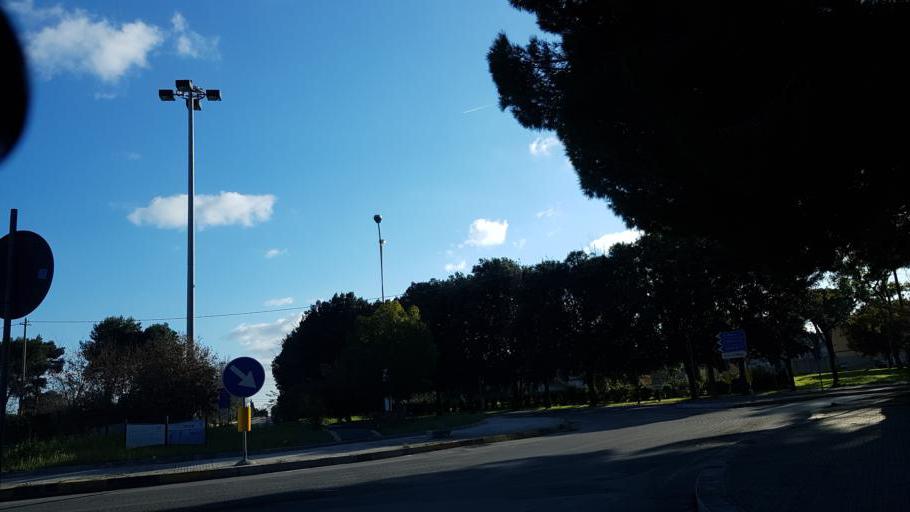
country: IT
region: Apulia
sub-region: Provincia di Brindisi
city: La Rosa
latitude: 40.6098
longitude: 17.9537
